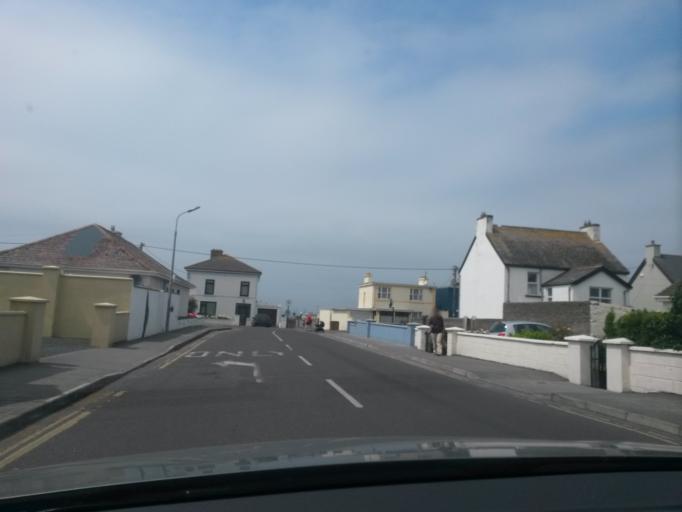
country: IE
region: Munster
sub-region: Ciarrai
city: Ballybunnion
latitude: 52.5088
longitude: -9.6766
